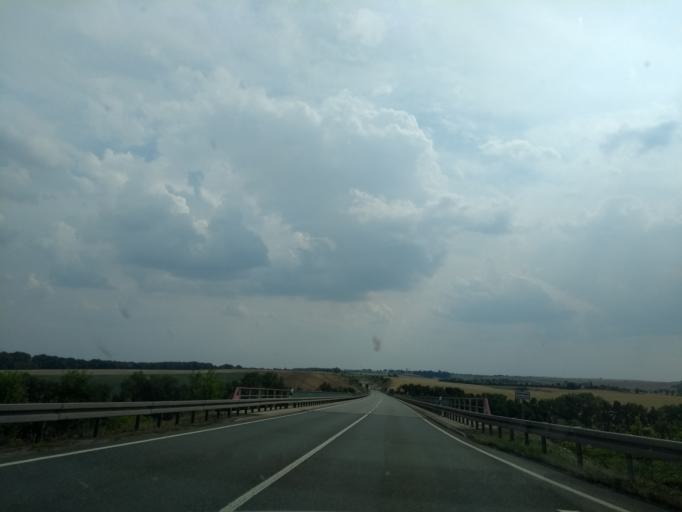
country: DE
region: Thuringia
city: Schwaara
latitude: 50.9193
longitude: 12.1342
